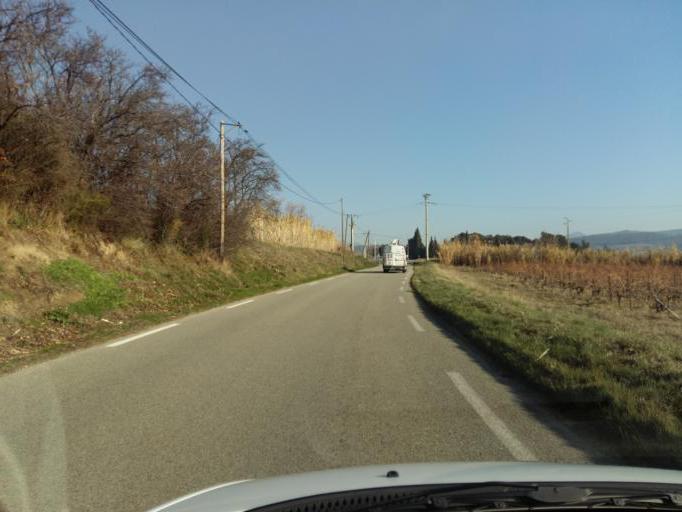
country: FR
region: Provence-Alpes-Cote d'Azur
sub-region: Departement du Vaucluse
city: Vaison-la-Romaine
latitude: 44.2542
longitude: 5.0211
